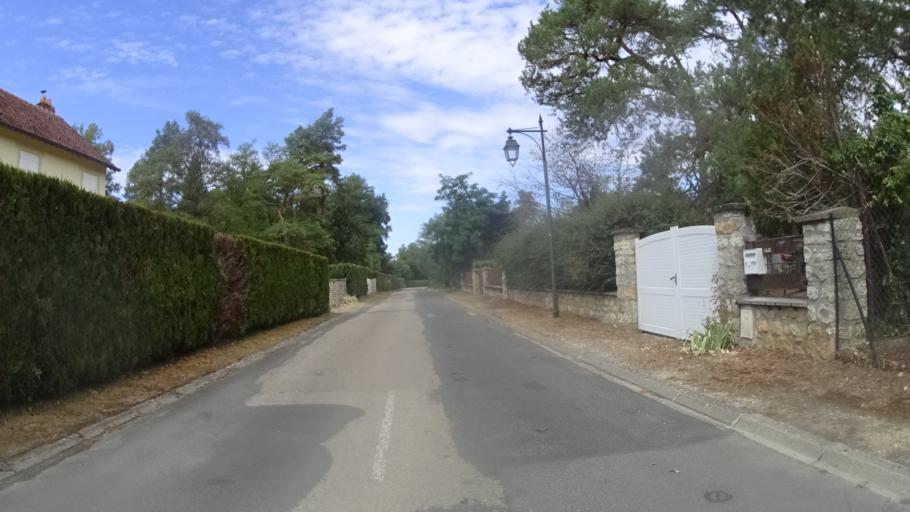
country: FR
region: Centre
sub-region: Departement du Loiret
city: Malesherbes
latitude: 48.2574
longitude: 2.4303
